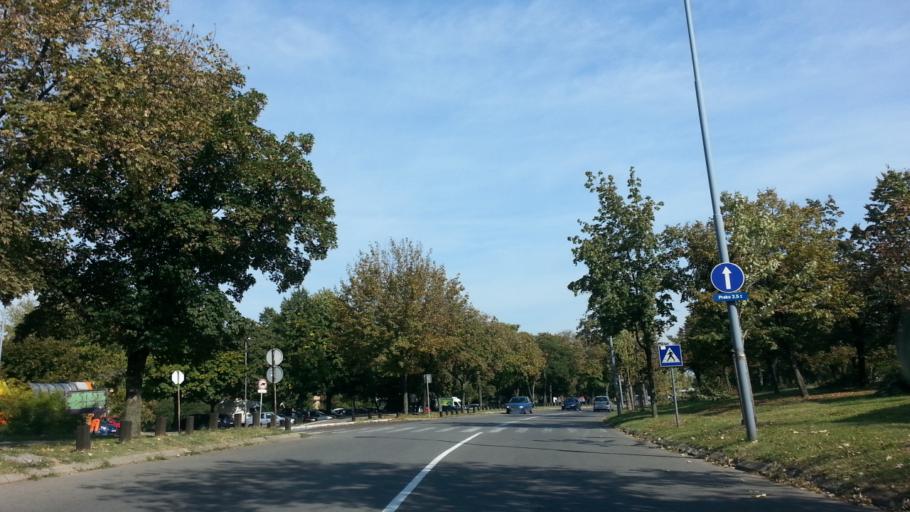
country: RS
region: Central Serbia
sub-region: Belgrade
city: Rakovica
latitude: 44.7438
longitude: 20.4221
